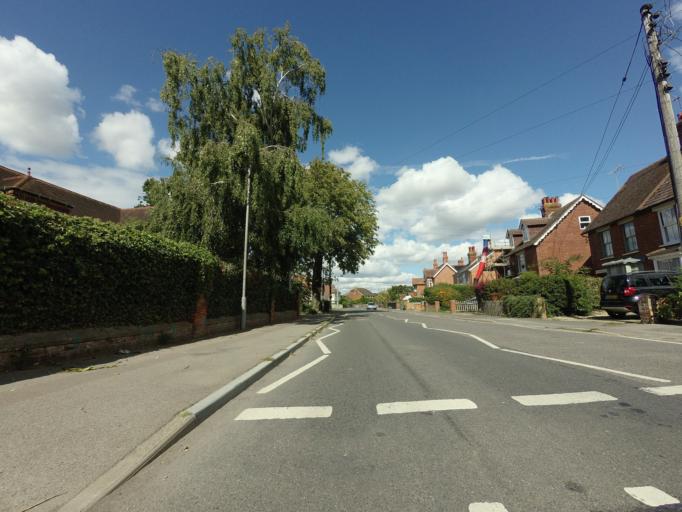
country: GB
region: England
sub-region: Kent
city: Marden
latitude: 51.1732
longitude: 0.4881
